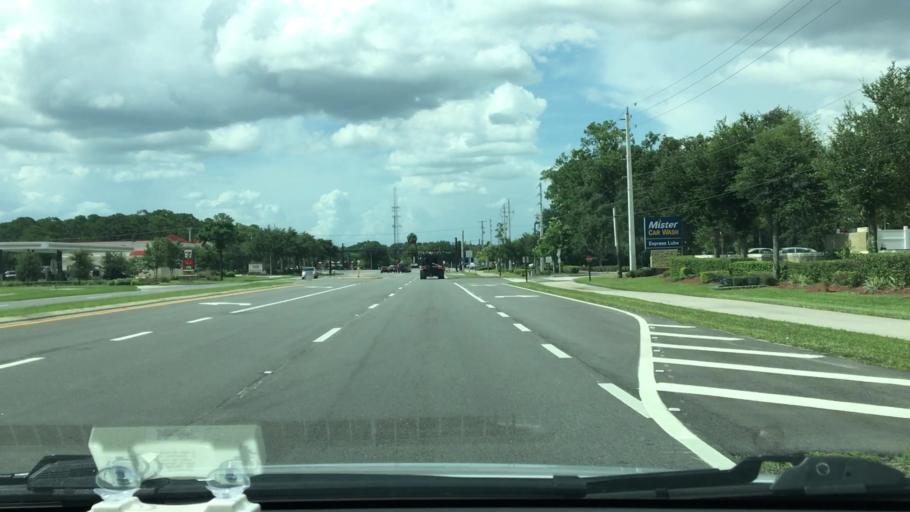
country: US
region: Florida
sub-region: Seminole County
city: Lake Mary
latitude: 28.8090
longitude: -81.3310
